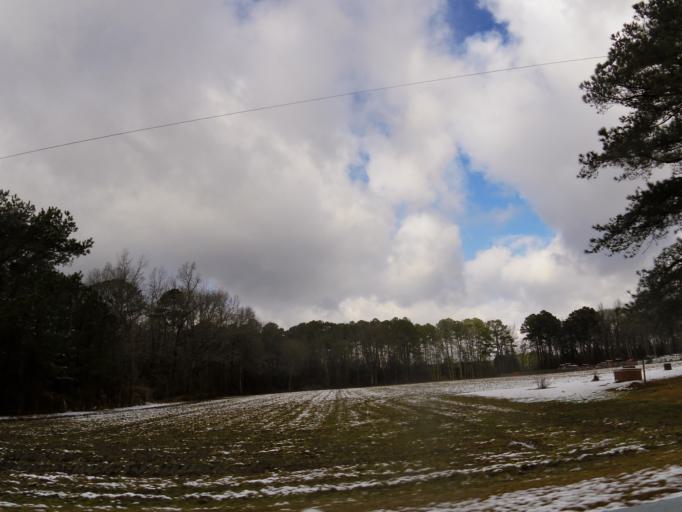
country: US
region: North Carolina
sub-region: Wilson County
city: Lucama
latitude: 35.7044
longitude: -78.0338
